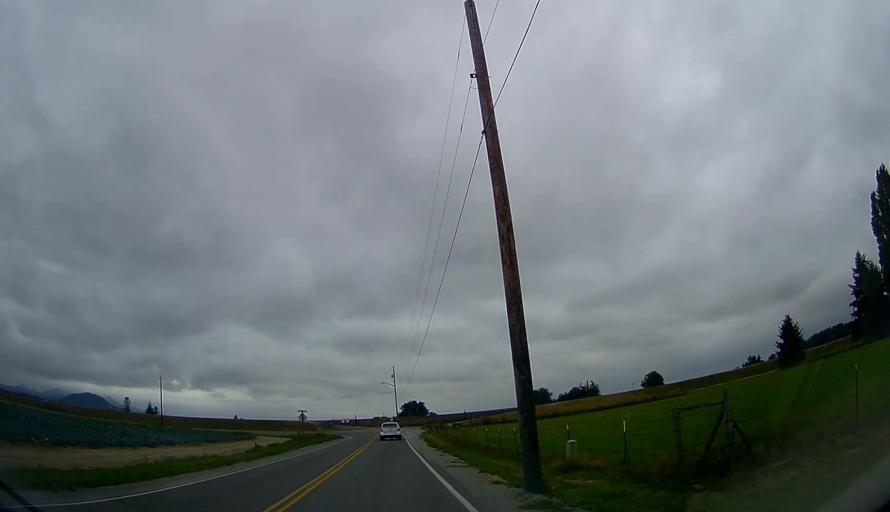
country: US
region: Washington
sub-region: Skagit County
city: Mount Vernon
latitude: 48.4494
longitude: -122.3572
